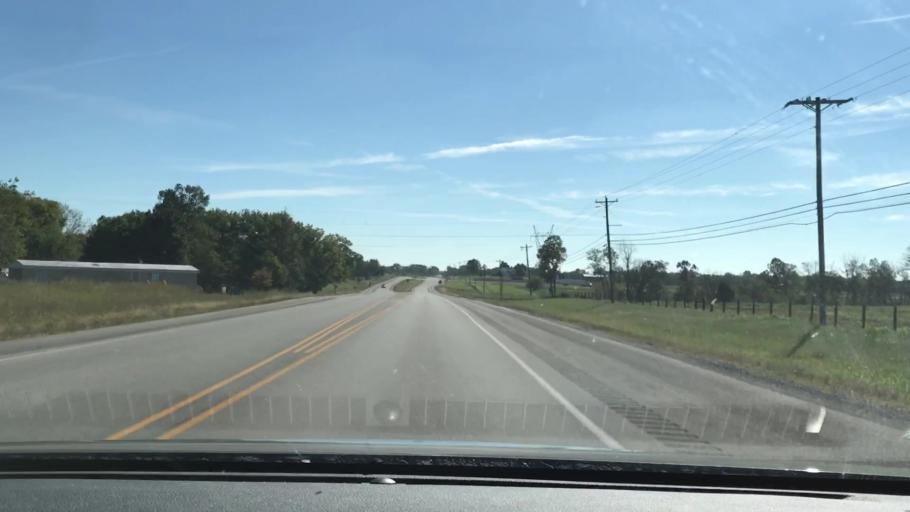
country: US
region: Kentucky
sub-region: Christian County
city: Hopkinsville
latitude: 36.8593
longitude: -87.4306
